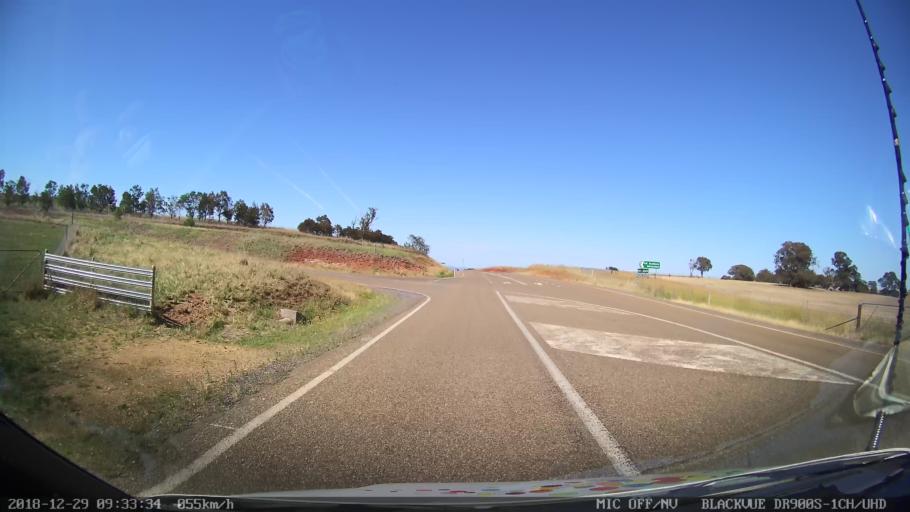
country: AU
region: New South Wales
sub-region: Upper Lachlan Shire
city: Crookwell
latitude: -34.6263
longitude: 149.3454
